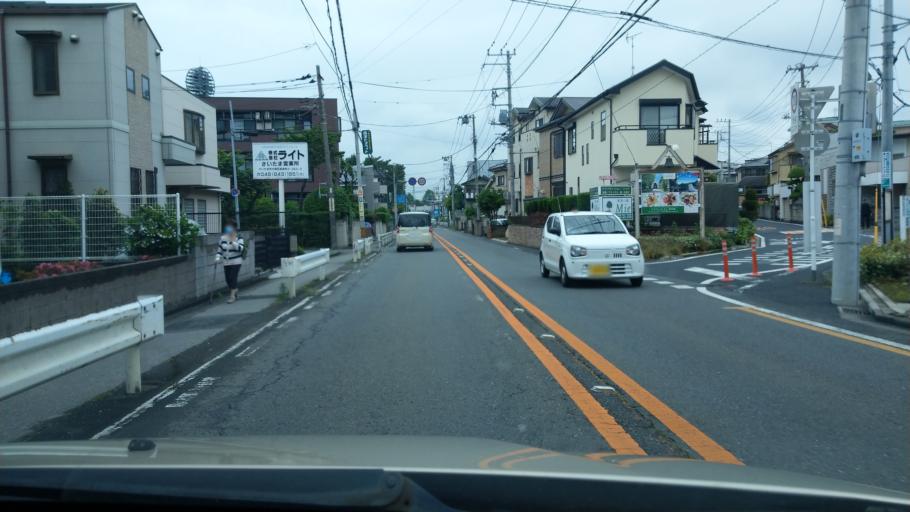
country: JP
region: Saitama
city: Saitama
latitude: 35.9140
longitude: 139.6344
